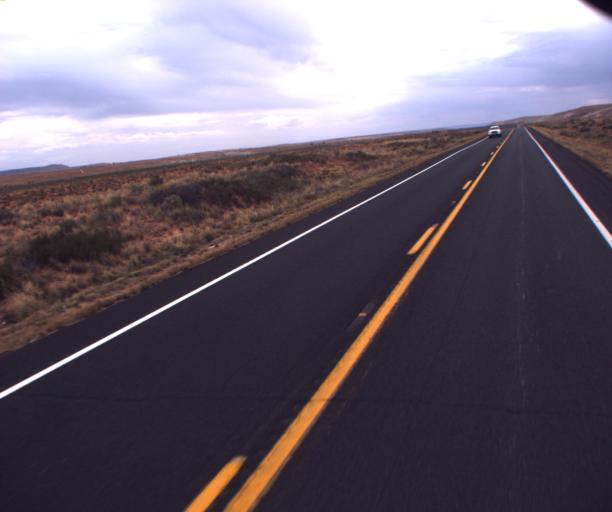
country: US
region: Arizona
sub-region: Coconino County
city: Kaibito
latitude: 36.3600
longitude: -110.9033
